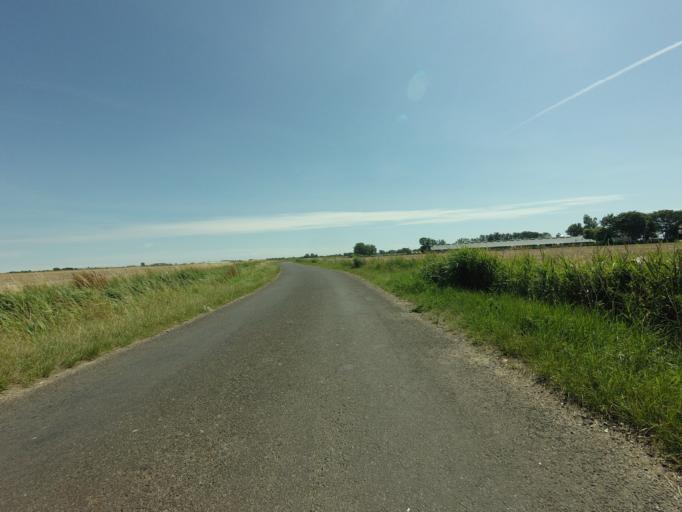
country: GB
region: England
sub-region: Kent
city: Lydd
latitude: 50.9703
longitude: 0.8973
